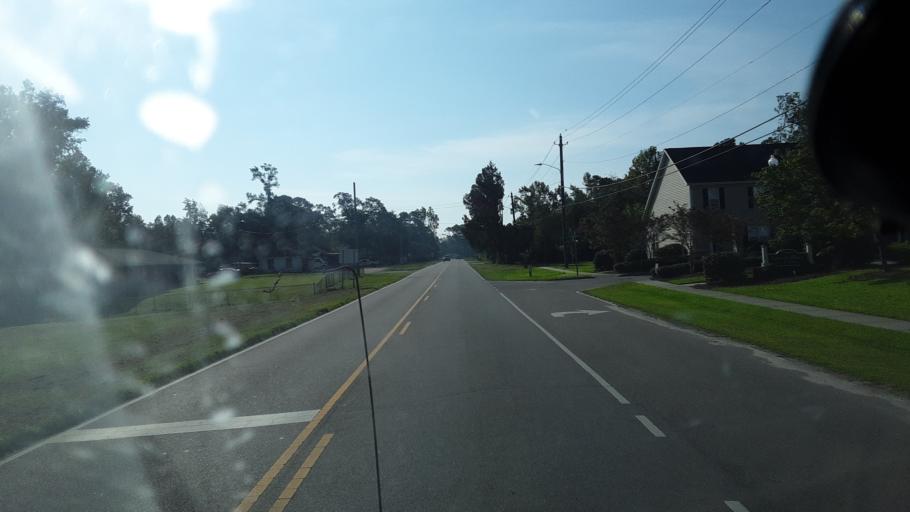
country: US
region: North Carolina
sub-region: Brunswick County
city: Leland
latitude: 34.2553
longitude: -78.0429
